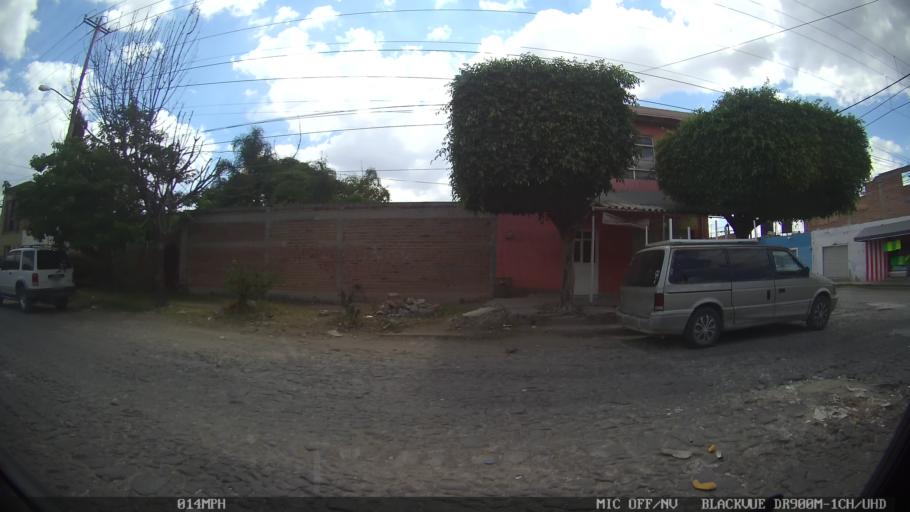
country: MX
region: Jalisco
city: Tlaquepaque
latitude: 20.6700
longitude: -103.2605
